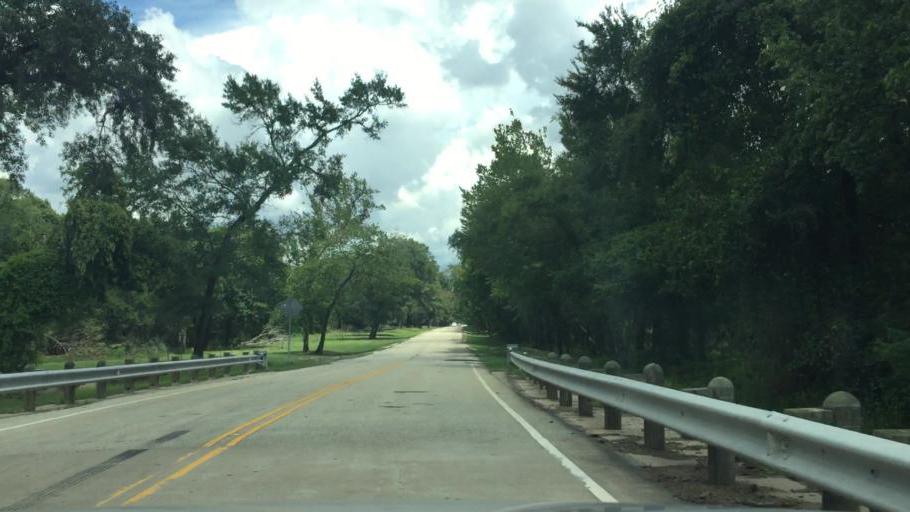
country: US
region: Texas
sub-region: Harris County
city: Jersey Village
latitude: 29.8134
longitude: -95.6288
